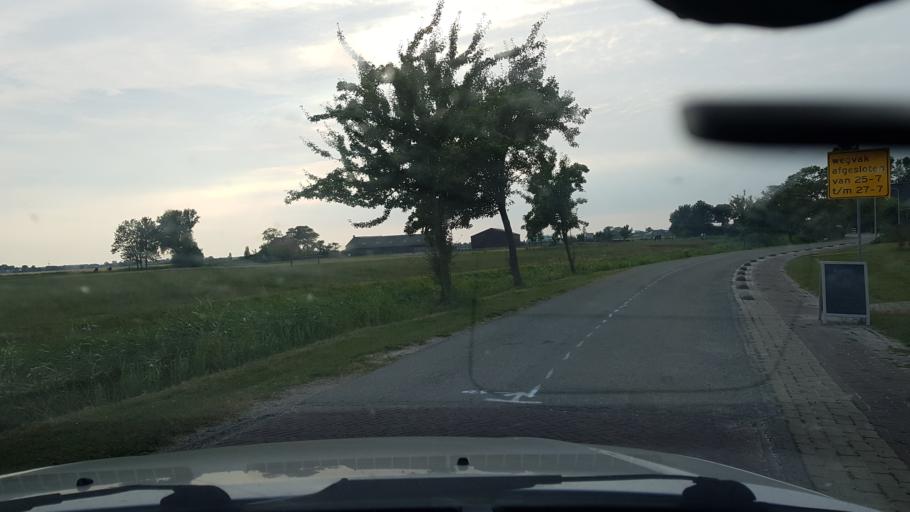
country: NL
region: Friesland
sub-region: Gemeente Dongeradeel
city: Holwerd
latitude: 53.3455
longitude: 5.8777
